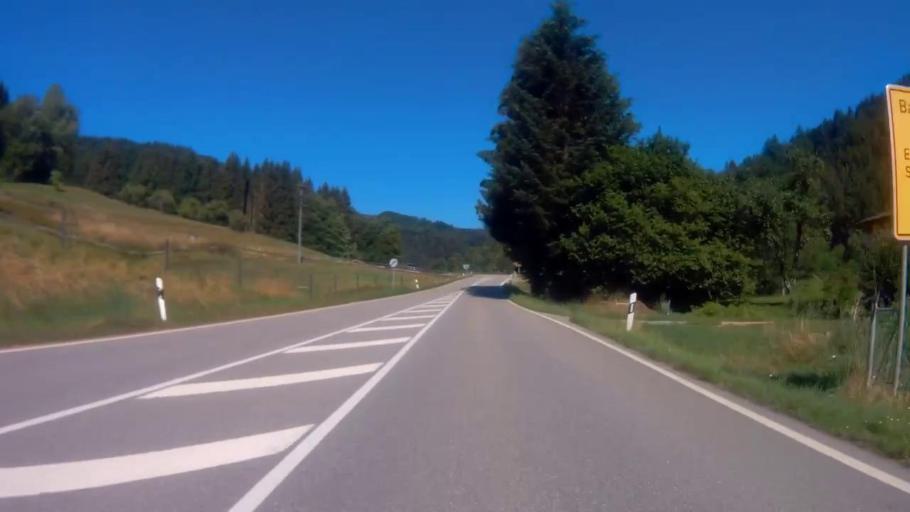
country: DE
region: Baden-Wuerttemberg
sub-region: Freiburg Region
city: Hausen
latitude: 47.7207
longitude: 7.7897
